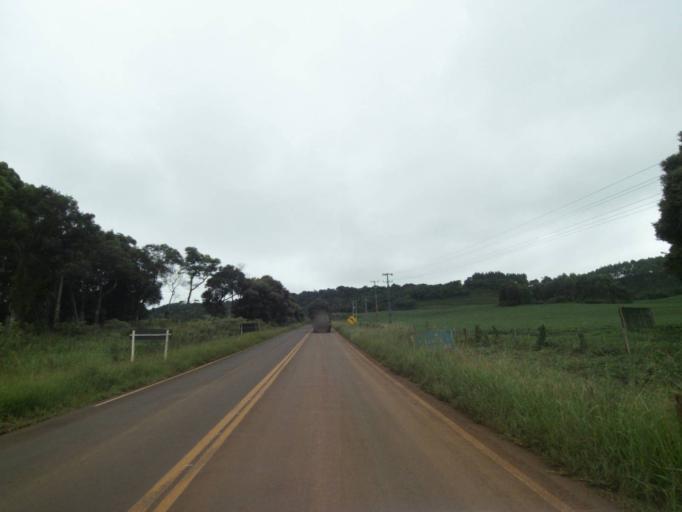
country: BR
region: Parana
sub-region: Pitanga
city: Pitanga
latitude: -24.9238
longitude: -51.8717
